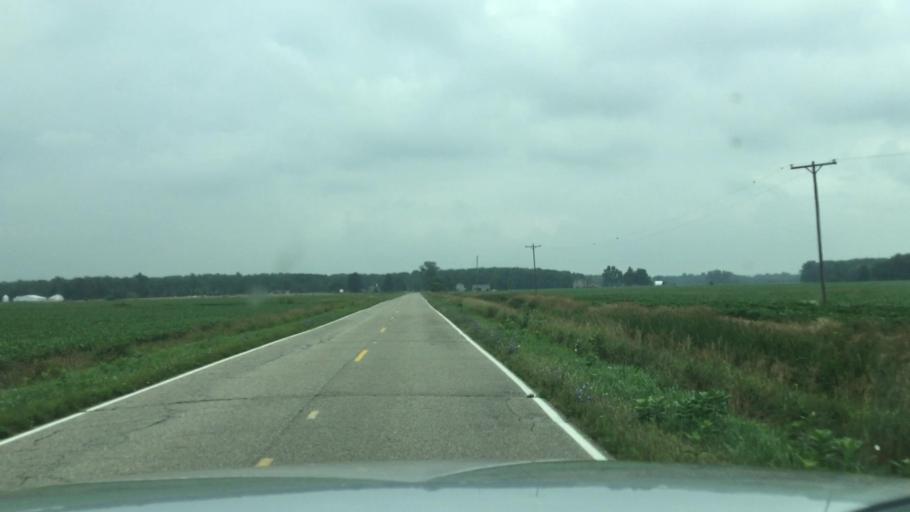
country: US
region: Michigan
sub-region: Shiawassee County
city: New Haven
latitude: 43.0657
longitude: -84.2261
